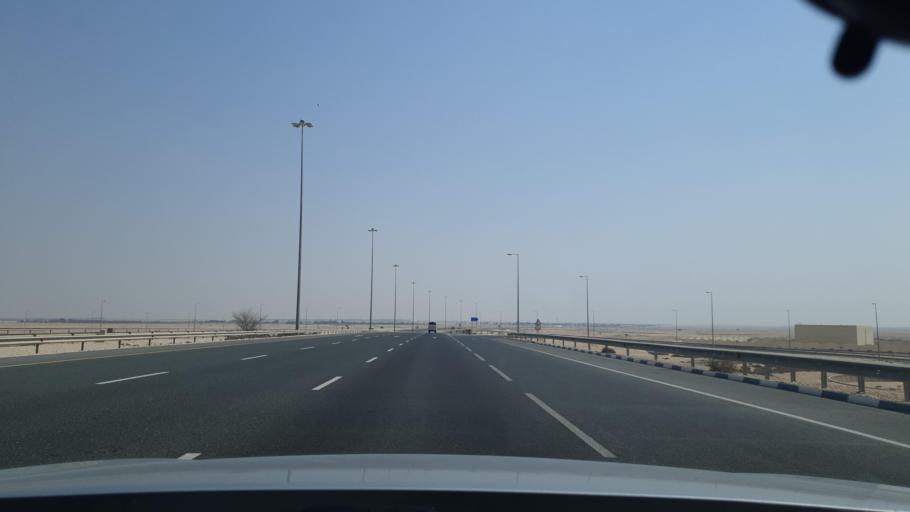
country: QA
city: Al Ghuwayriyah
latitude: 25.8286
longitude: 51.3506
